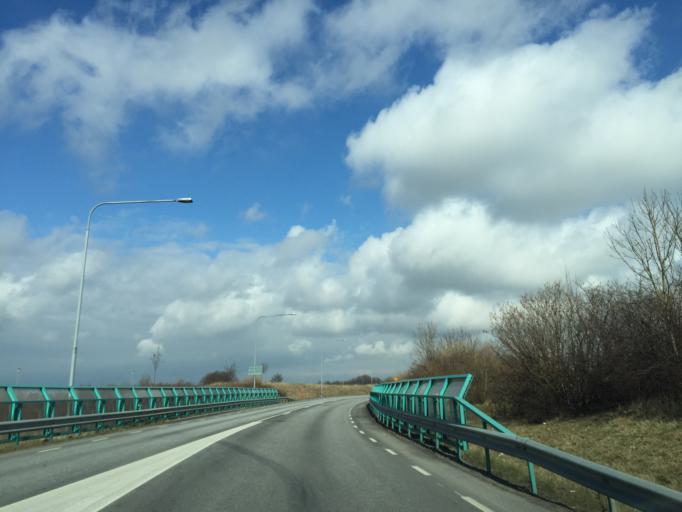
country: SE
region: Skane
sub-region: Burlovs Kommun
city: Arloev
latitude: 55.5895
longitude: 13.1048
